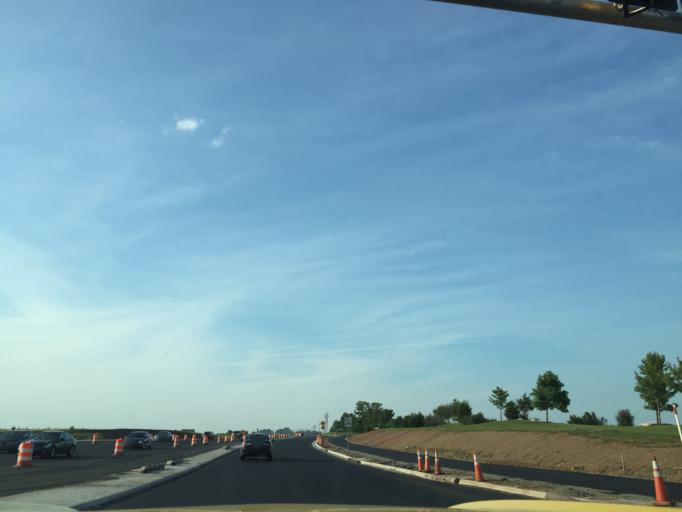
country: US
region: Virginia
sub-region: Loudoun County
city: University Center
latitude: 39.0282
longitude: -77.4482
